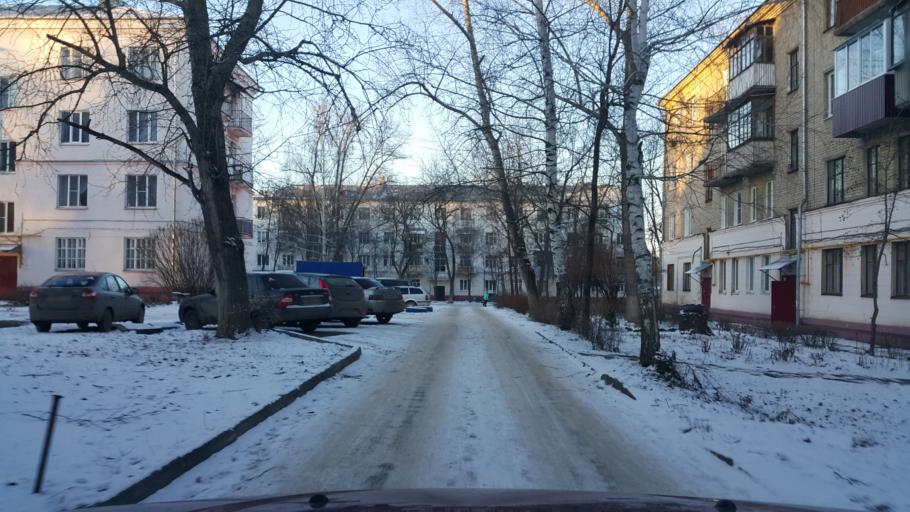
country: RU
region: Tambov
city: Pokrovo-Prigorodnoye
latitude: 52.7090
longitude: 41.3949
